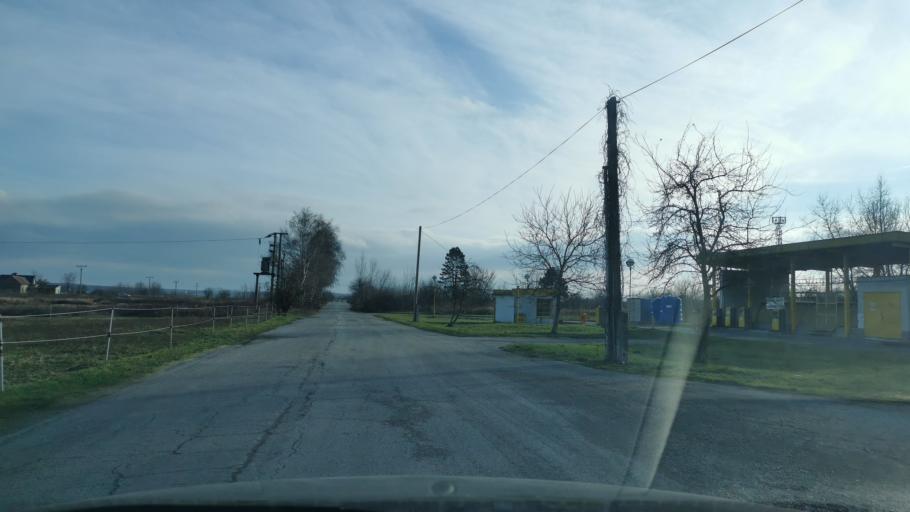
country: CZ
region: South Moravian
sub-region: Okres Hodonin
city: Mikulcice
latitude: 48.7817
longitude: 17.1045
